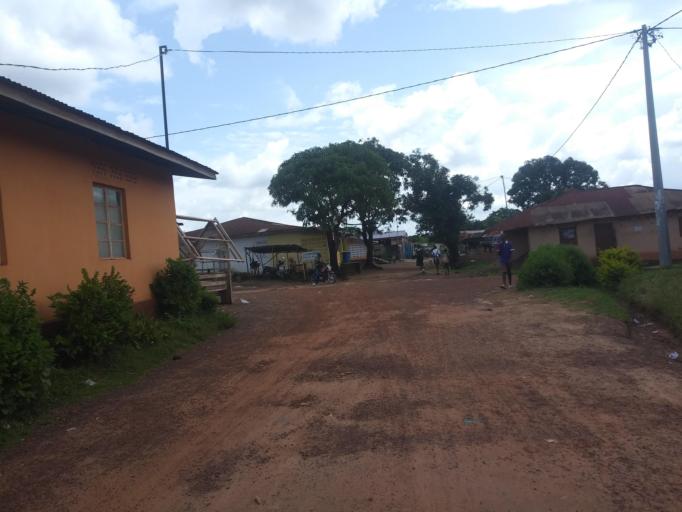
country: SL
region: Northern Province
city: Makeni
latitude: 8.8738
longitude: -12.0425
